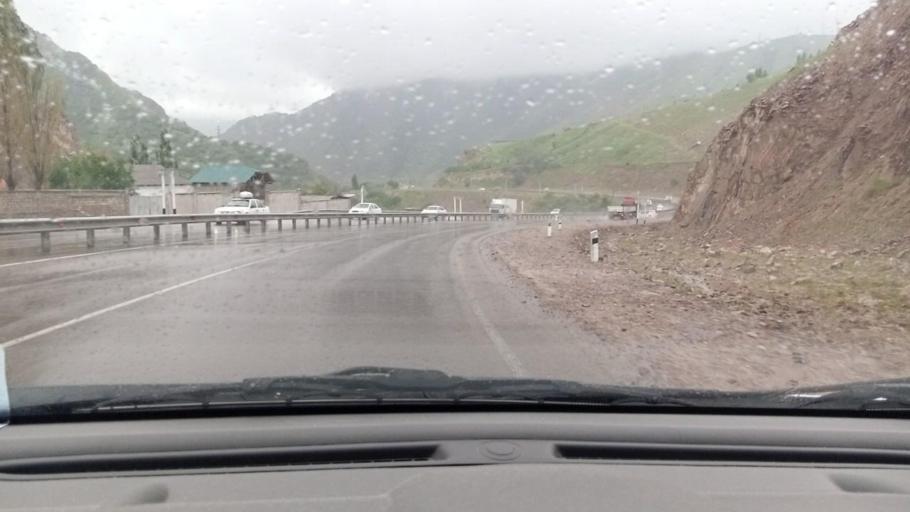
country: UZ
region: Toshkent
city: Angren
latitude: 41.1047
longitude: 70.3341
